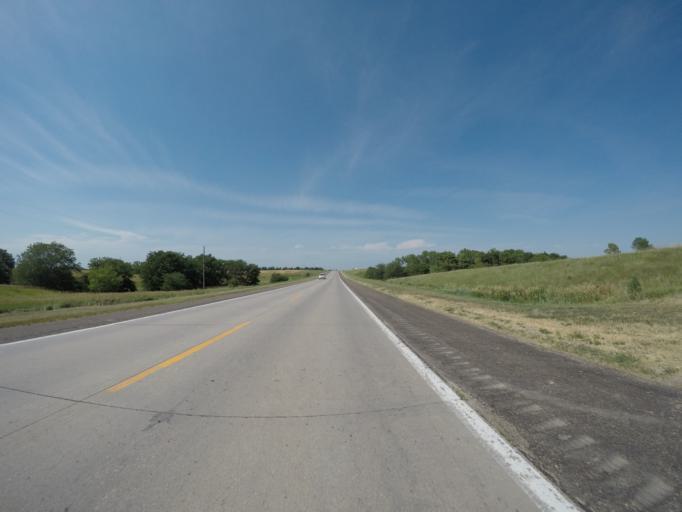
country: US
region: Nebraska
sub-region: Adams County
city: Hastings
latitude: 40.3722
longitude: -98.4396
